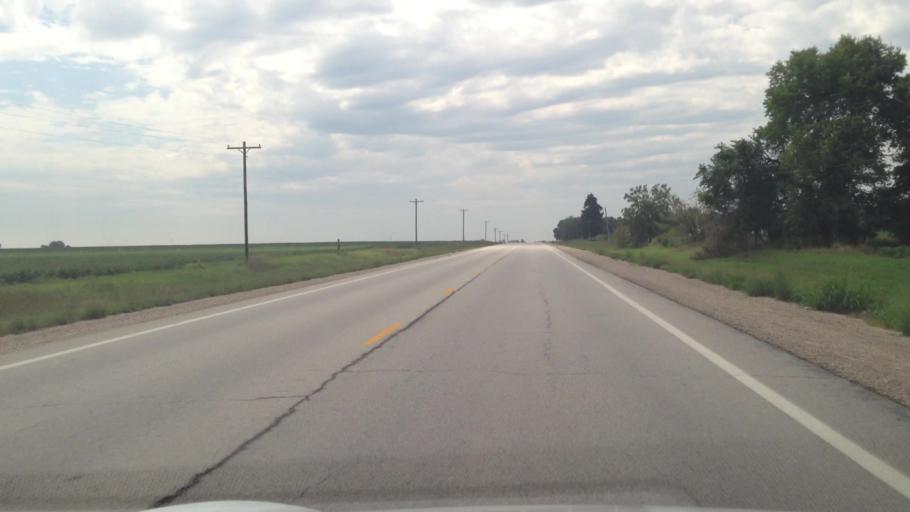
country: US
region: Kansas
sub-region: Anderson County
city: Garnett
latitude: 38.1042
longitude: -95.2430
